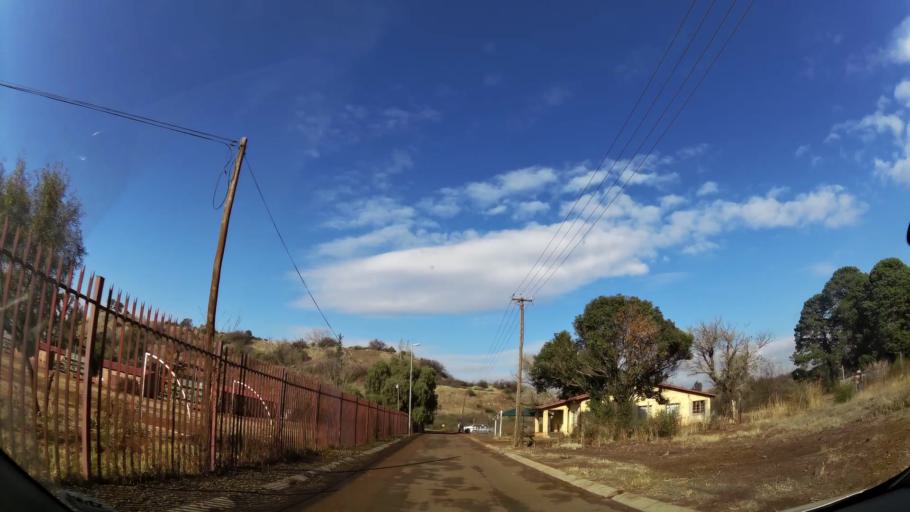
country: ZA
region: Gauteng
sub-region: Sedibeng District Municipality
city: Meyerton
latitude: -26.5059
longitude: 28.0687
